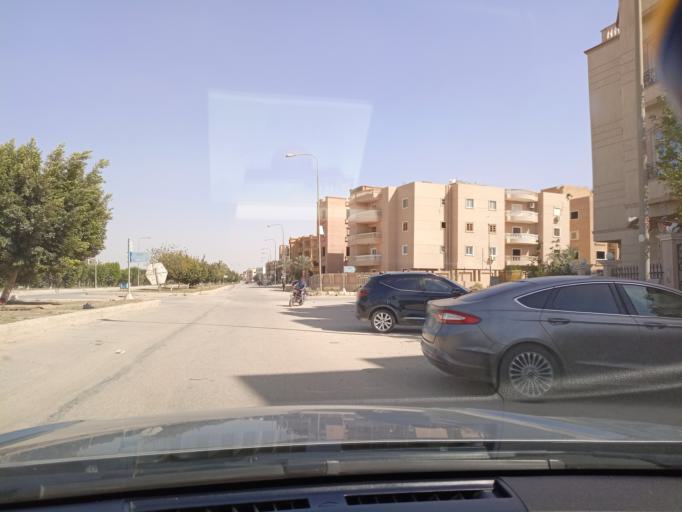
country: EG
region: Muhafazat al Qalyubiyah
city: Al Khankah
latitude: 30.2297
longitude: 31.4427
